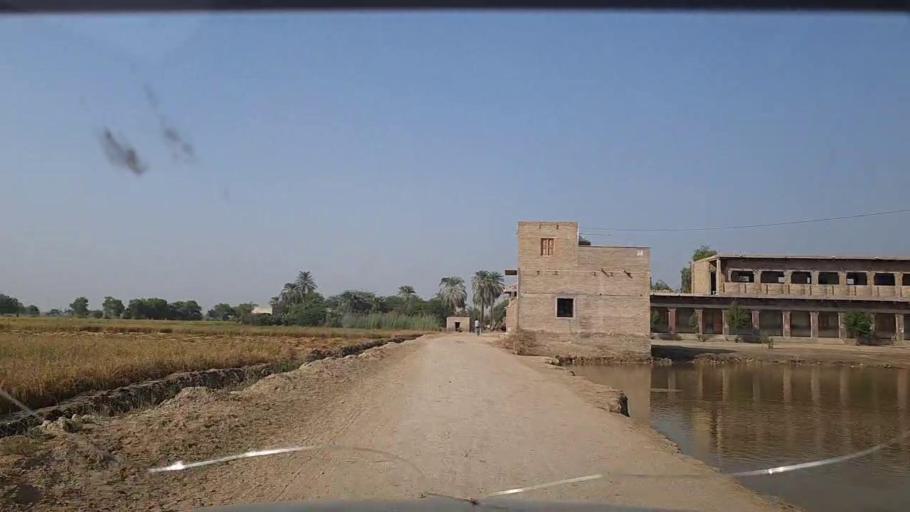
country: PK
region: Sindh
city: Shikarpur
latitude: 28.1191
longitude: 68.5787
